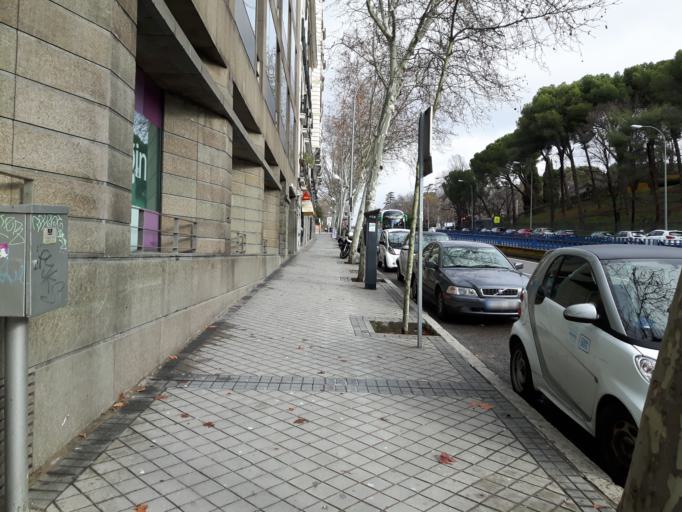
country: ES
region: Madrid
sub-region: Provincia de Madrid
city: Retiro
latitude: 40.4083
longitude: -3.6887
